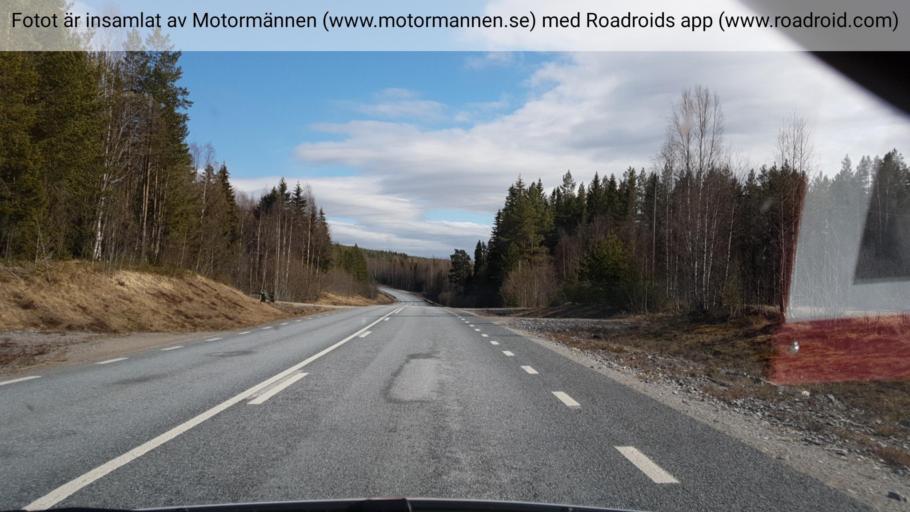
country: SE
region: Vaesternorrland
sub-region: Solleftea Kommun
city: As
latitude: 63.4179
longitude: 16.9570
